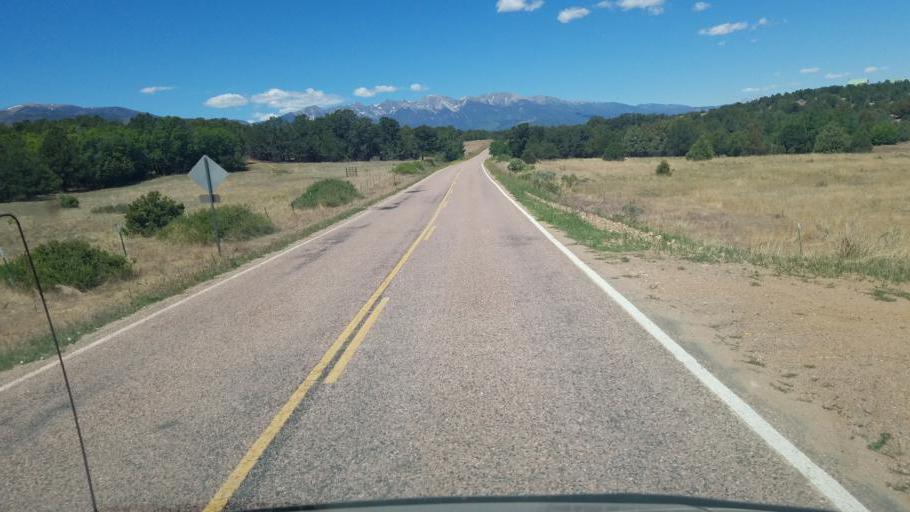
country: US
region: Colorado
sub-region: Custer County
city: Westcliffe
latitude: 38.3094
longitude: -105.6409
